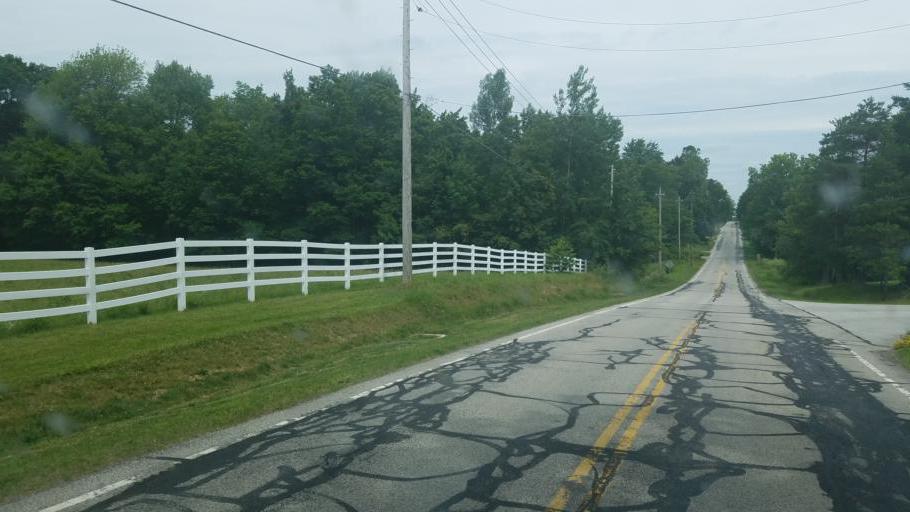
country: US
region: Ohio
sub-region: Geauga County
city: Bainbridge
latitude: 41.3898
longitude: -81.2463
